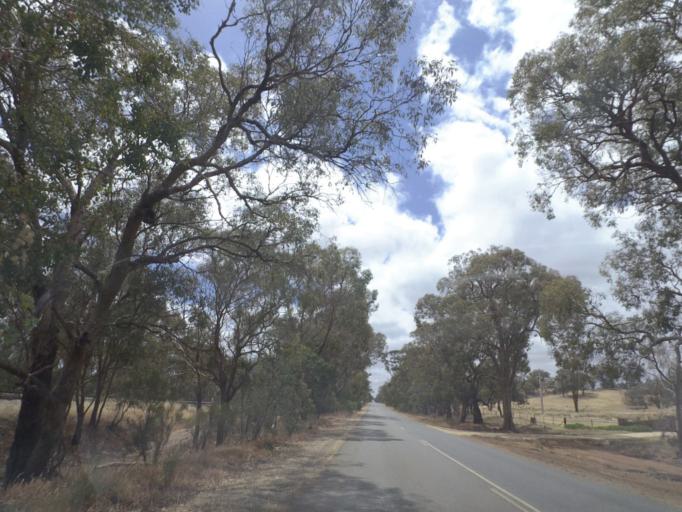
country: AU
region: Victoria
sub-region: Murrindindi
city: Kinglake West
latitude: -36.9217
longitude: 145.1988
